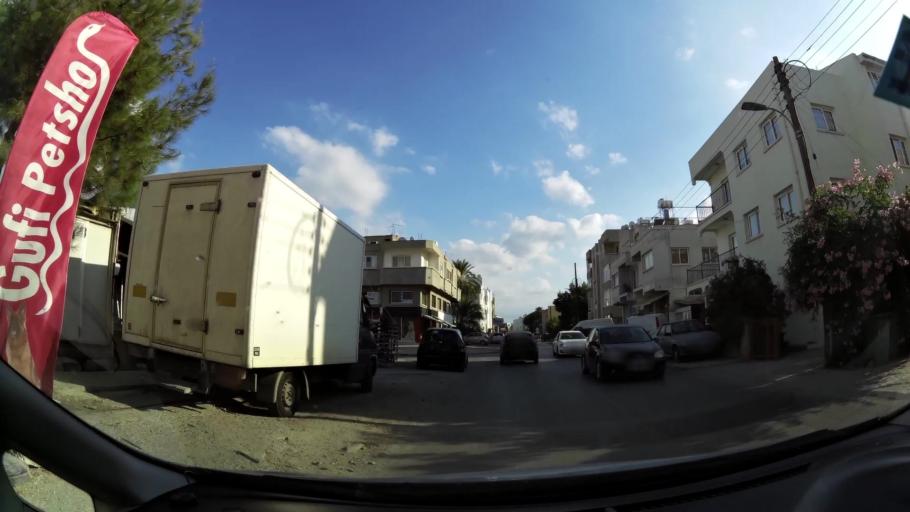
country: CY
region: Lefkosia
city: Nicosia
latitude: 35.1975
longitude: 33.3641
